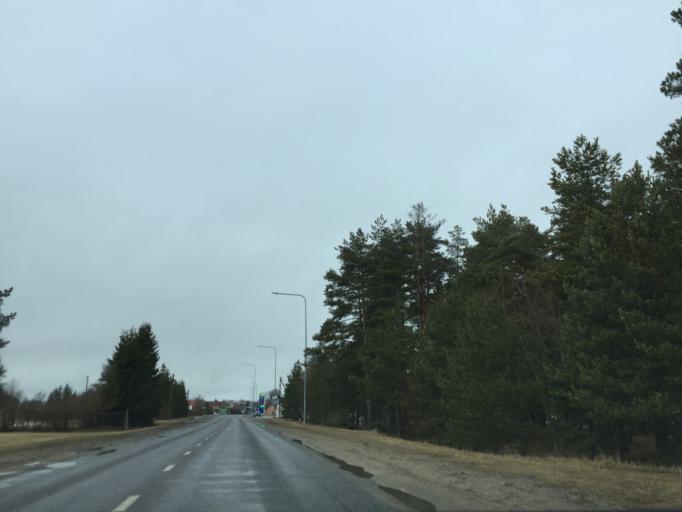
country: EE
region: Laeaene
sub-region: Haapsalu linn
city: Haapsalu
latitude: 58.9238
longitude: 23.5468
